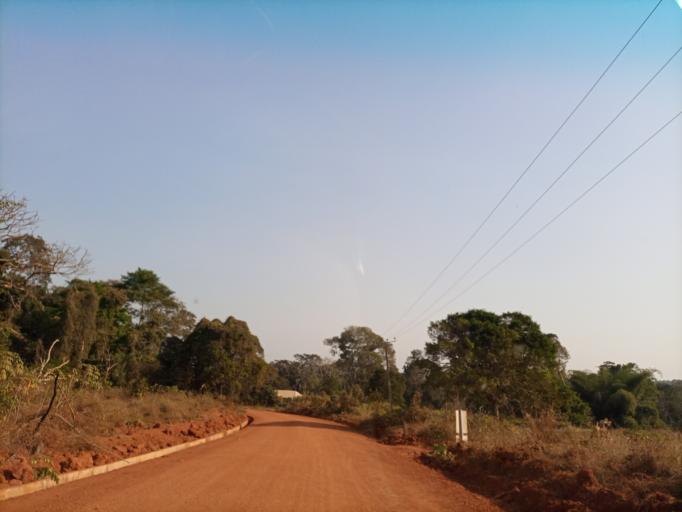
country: NG
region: Enugu
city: Opi
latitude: 6.7614
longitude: 7.3979
